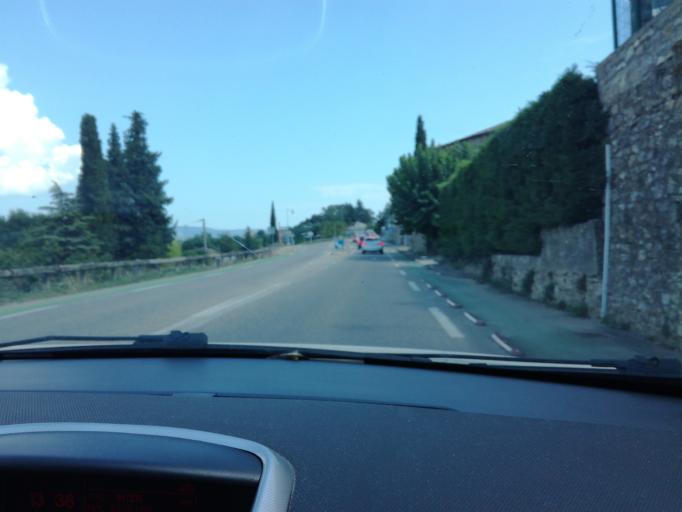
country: FR
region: Rhone-Alpes
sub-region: Departement de l'Ardeche
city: Saint-Sernin
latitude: 44.5220
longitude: 4.3996
